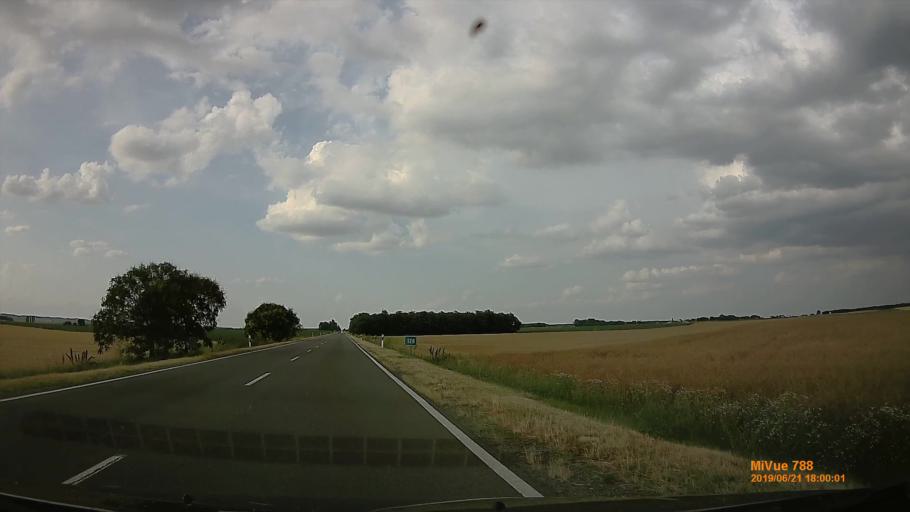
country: HU
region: Tolna
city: Fadd
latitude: 46.4697
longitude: 18.7824
